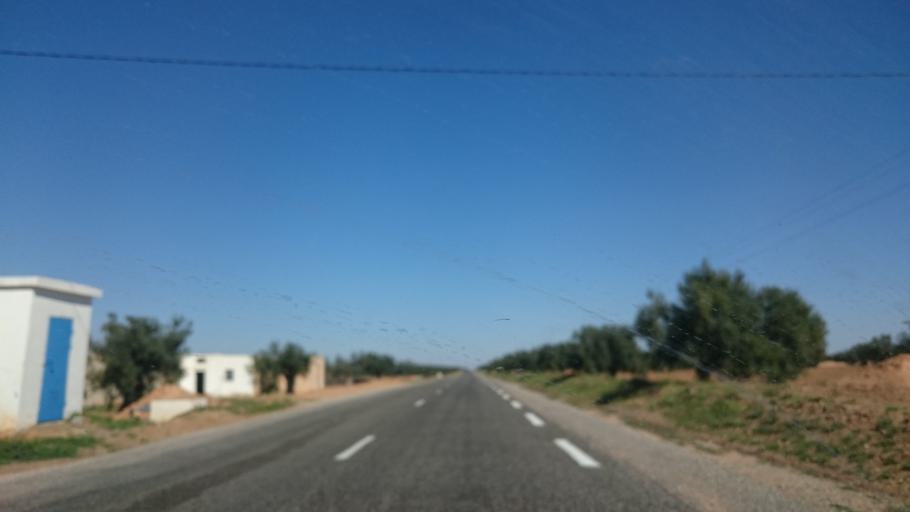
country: TN
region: Safaqis
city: Sfax
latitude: 34.8386
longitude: 10.4588
